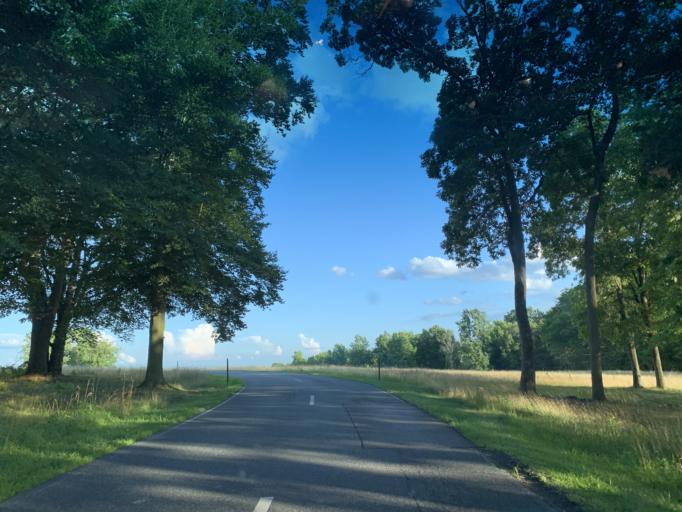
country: US
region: Maryland
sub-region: Harford County
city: Havre de Grace
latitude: 39.5395
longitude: -76.1332
